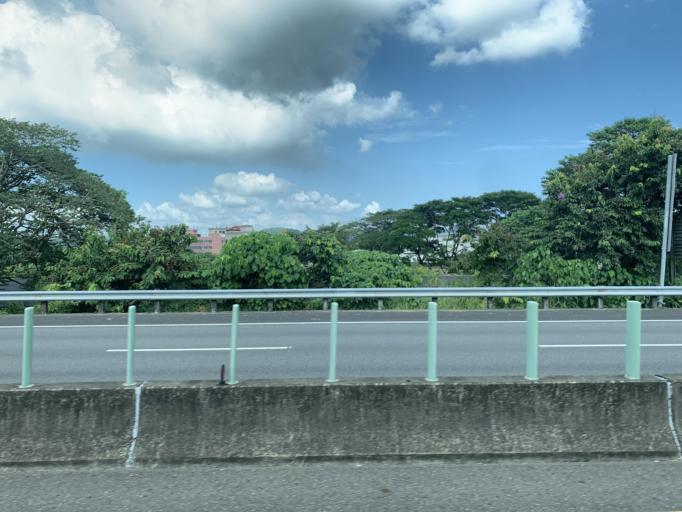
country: TW
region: Taiwan
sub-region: Pingtung
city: Pingtung
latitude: 22.8666
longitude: 120.4930
